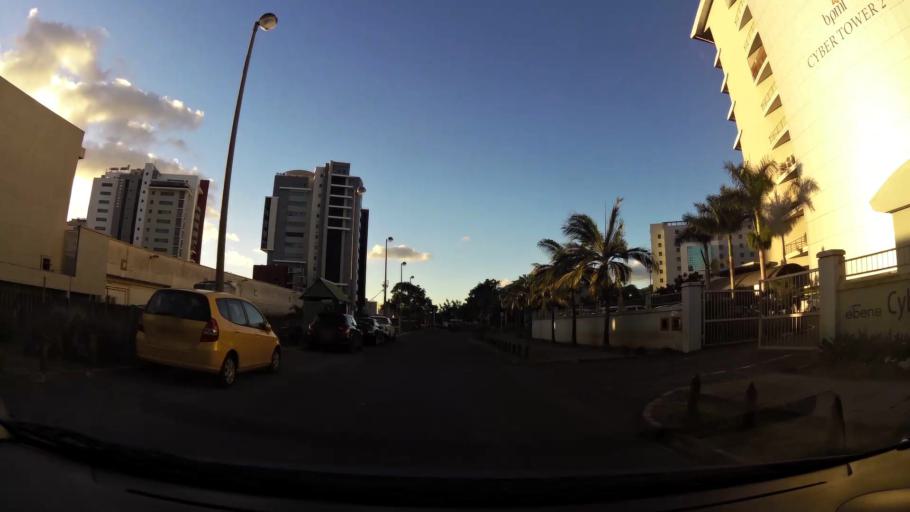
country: MU
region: Plaines Wilhems
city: Ebene
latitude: -20.2438
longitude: 57.4890
